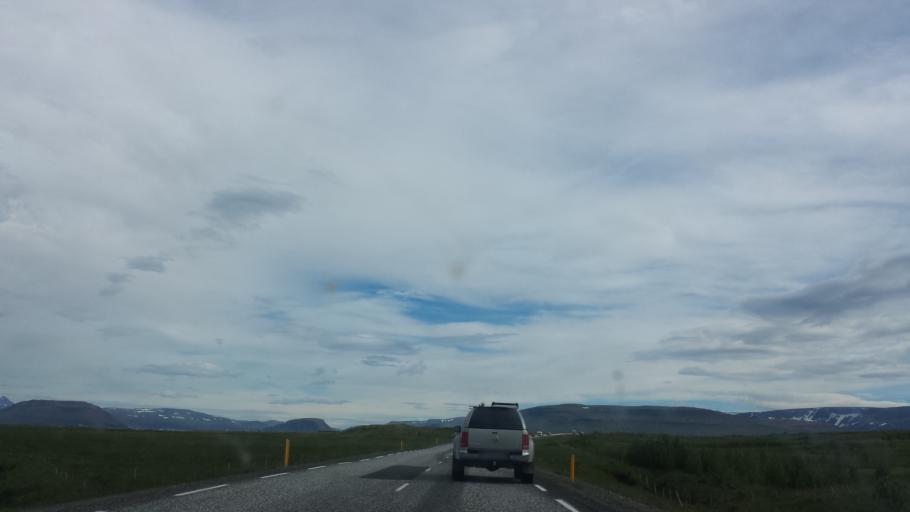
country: IS
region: West
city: Borgarnes
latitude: 64.3749
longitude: -21.8453
